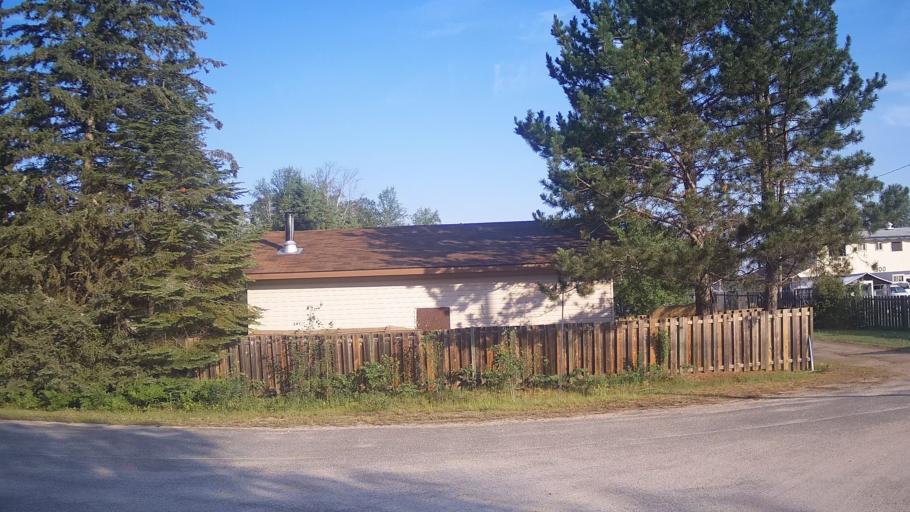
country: CA
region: Ontario
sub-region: Rainy River District
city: Atikokan
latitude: 49.3982
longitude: -91.6676
